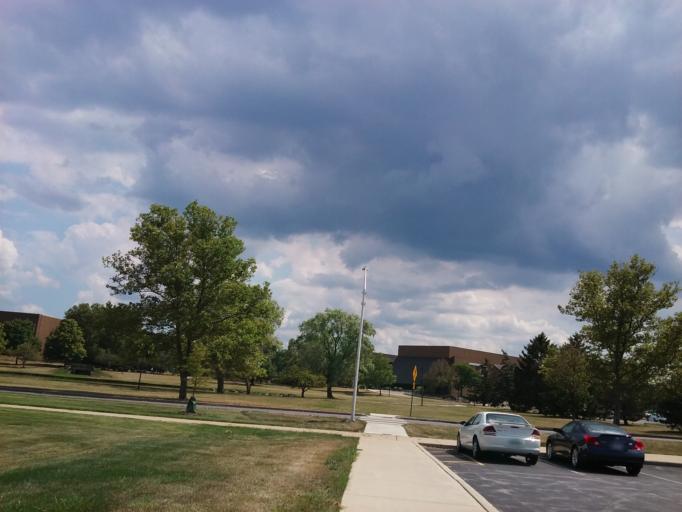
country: US
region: Ohio
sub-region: Wood County
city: Bowling Green
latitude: 41.3812
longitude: -83.6330
